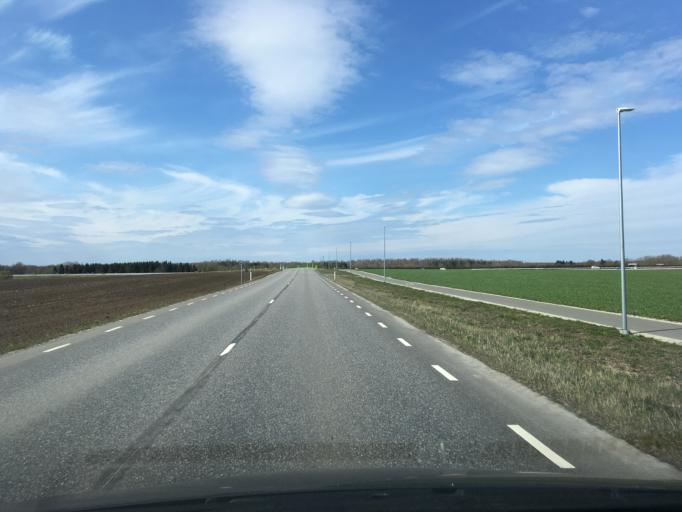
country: EE
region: Harju
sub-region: Maardu linn
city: Maardu
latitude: 59.4477
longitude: 25.0643
